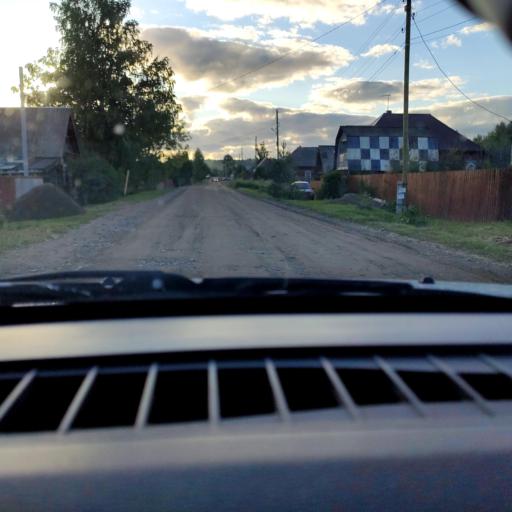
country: RU
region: Perm
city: Novyye Lyady
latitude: 58.1737
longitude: 56.5529
